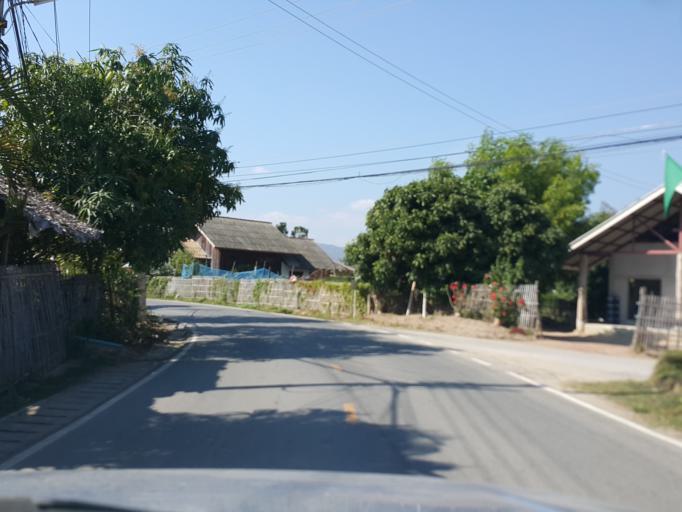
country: TH
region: Chiang Mai
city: Mae Wang
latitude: 18.5887
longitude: 98.8000
